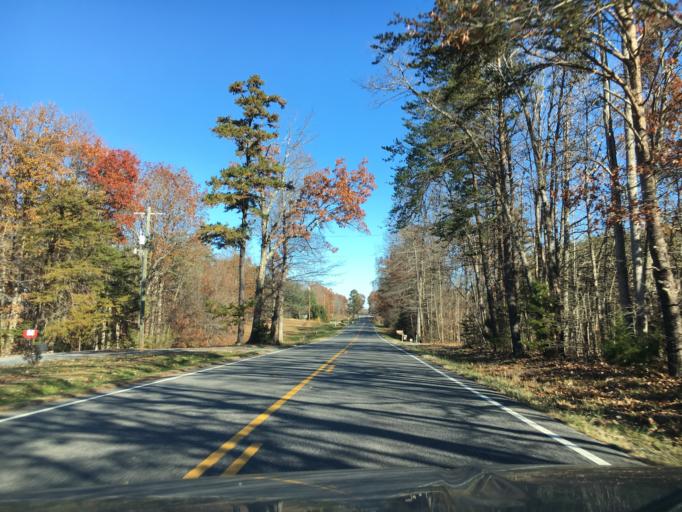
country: US
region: Virginia
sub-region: Appomattox County
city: Appomattox
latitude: 37.4426
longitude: -78.7185
